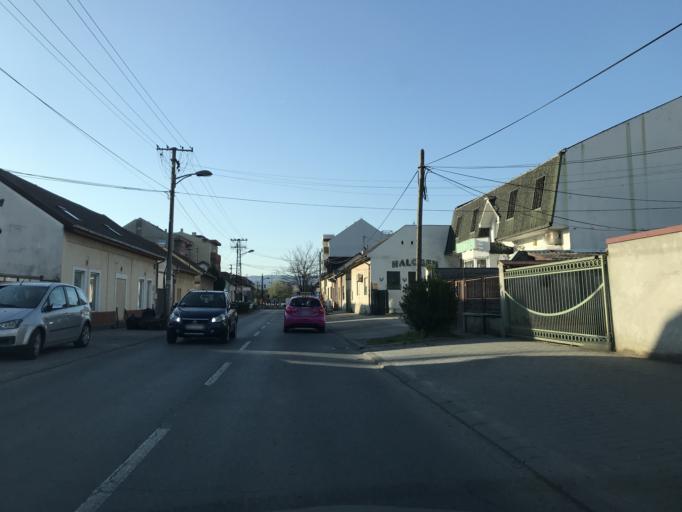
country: RS
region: Autonomna Pokrajina Vojvodina
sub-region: Juznobacki Okrug
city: Novi Sad
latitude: 45.2424
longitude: 19.8105
